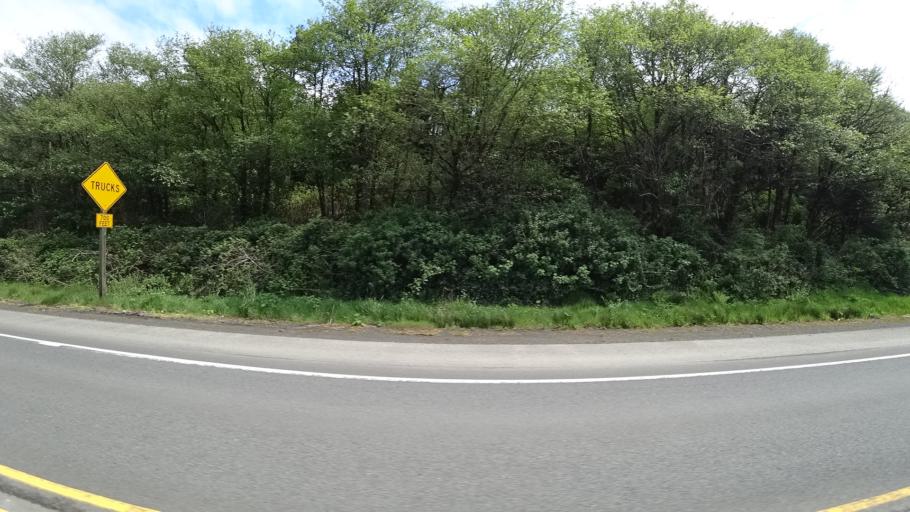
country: US
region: Oregon
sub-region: Lincoln County
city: Lincoln Beach
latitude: 44.8921
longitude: -124.0212
